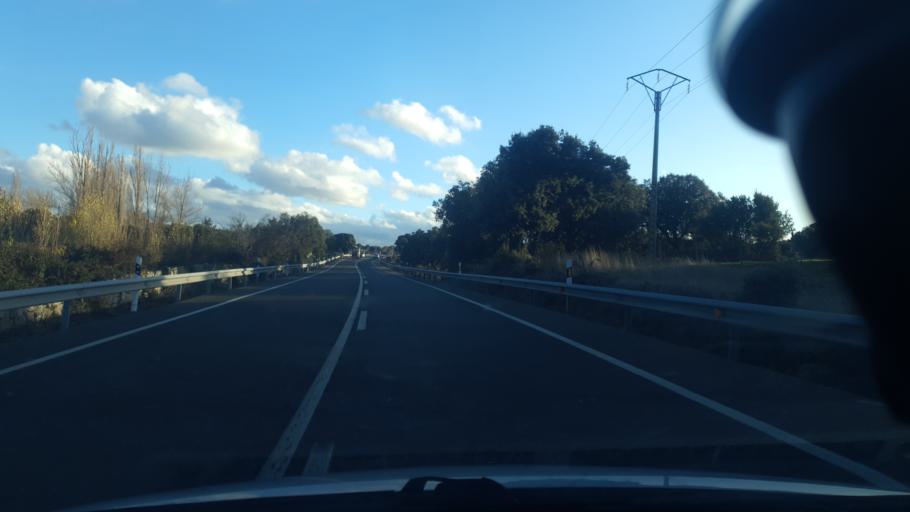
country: ES
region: Castille and Leon
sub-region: Provincia de Avila
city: Mingorria
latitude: 40.7299
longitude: -4.6759
